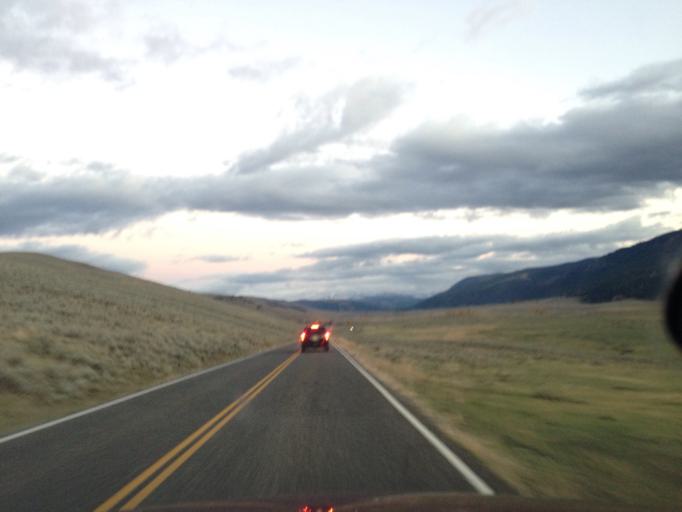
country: US
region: Montana
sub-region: Park County
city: Livingston
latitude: 44.9070
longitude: -110.2507
